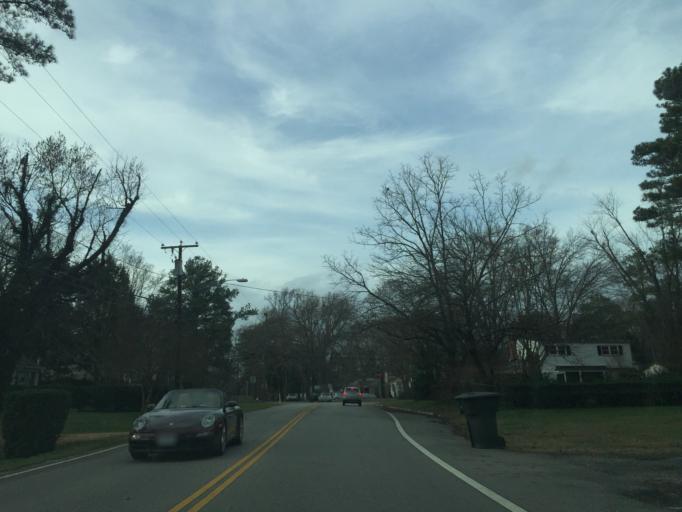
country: US
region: Virginia
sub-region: City of Newport News
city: Newport News
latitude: 37.0555
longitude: -76.4991
